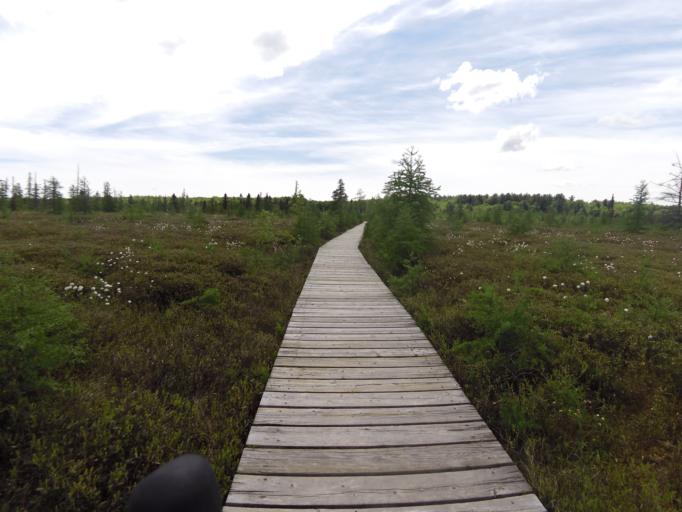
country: CA
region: Ontario
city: Ottawa
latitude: 45.3908
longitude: -75.5124
